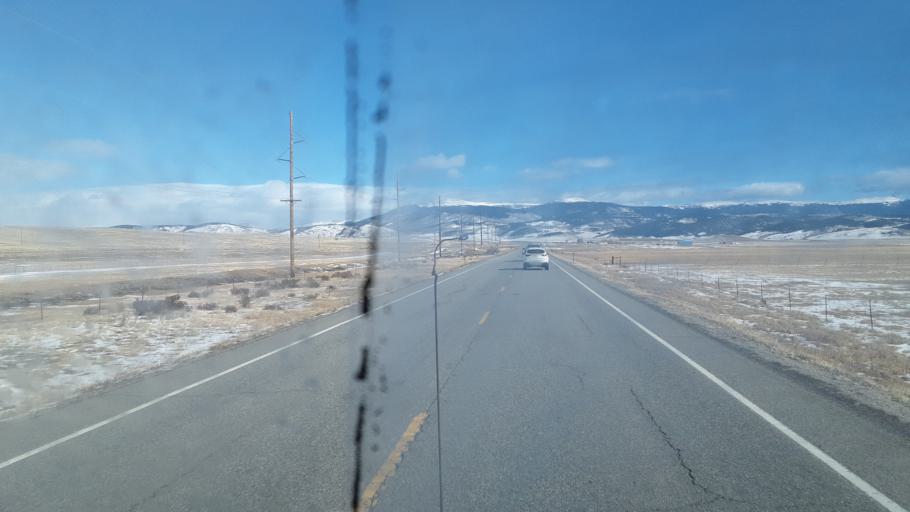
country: US
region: Colorado
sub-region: Park County
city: Fairplay
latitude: 39.3524
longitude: -105.8287
